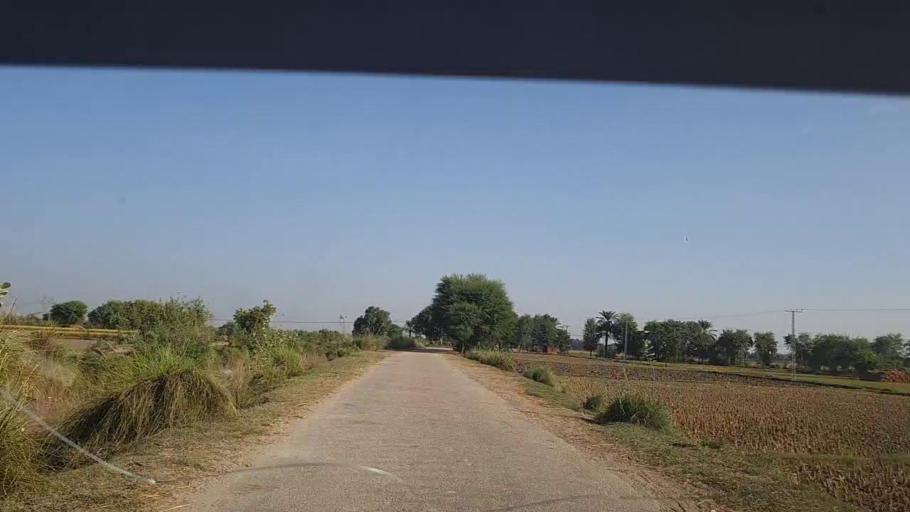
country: PK
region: Sindh
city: Larkana
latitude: 27.6226
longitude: 68.2430
